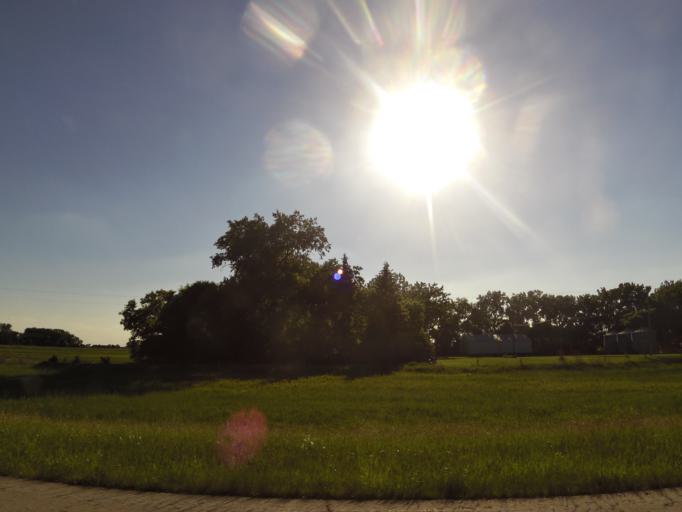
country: US
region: North Dakota
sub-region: Walsh County
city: Grafton
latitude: 48.3851
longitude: -97.1905
